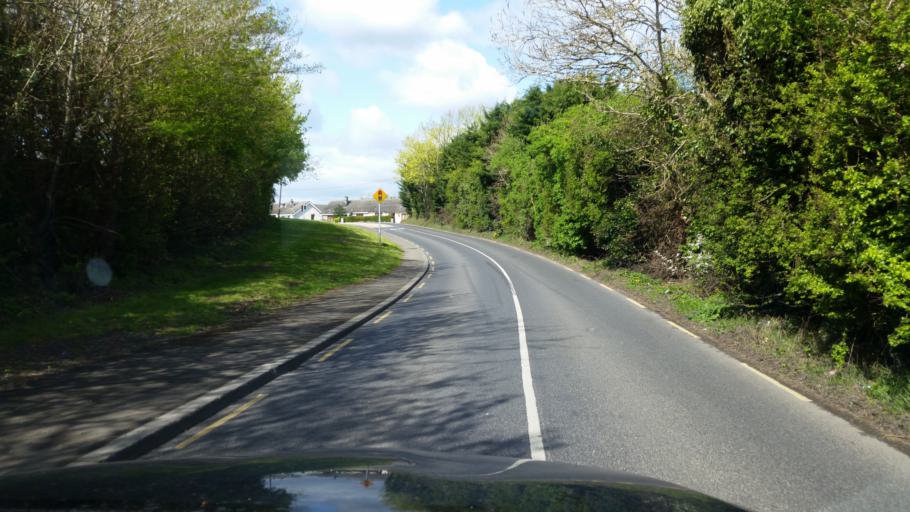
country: IE
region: Leinster
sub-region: Fingal County
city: Swords
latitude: 53.4877
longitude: -6.3027
